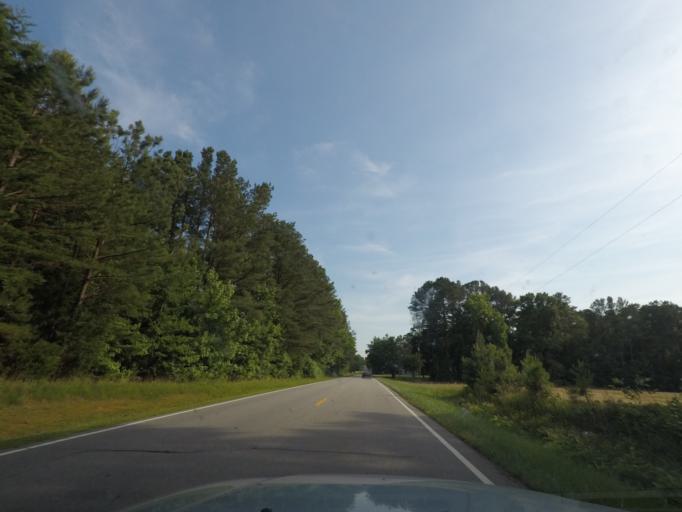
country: US
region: Virginia
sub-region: Mecklenburg County
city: Clarksville
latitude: 36.5067
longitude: -78.5376
